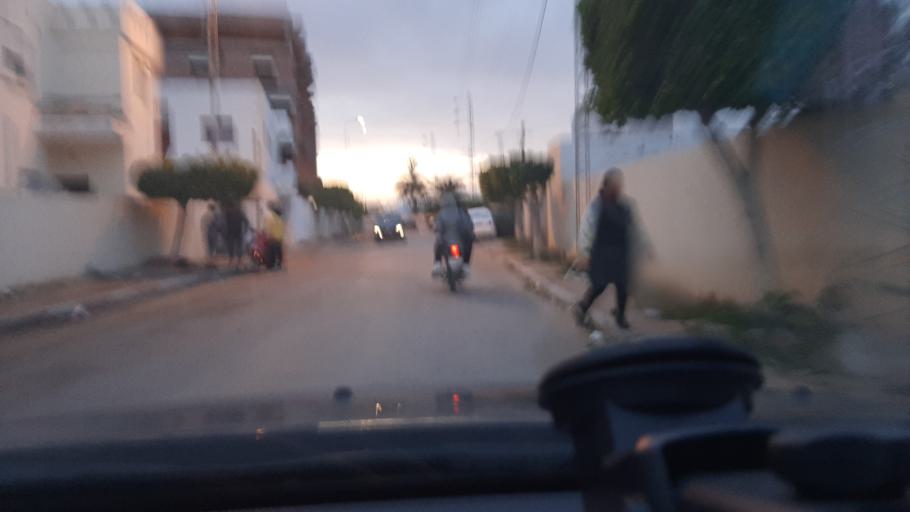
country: TN
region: Safaqis
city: Sfax
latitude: 34.7629
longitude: 10.6936
